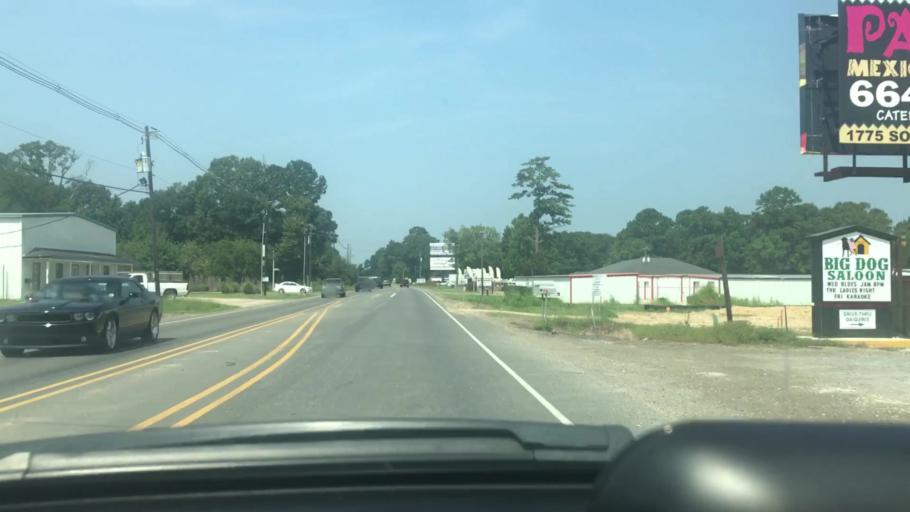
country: US
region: Louisiana
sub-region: Livingston Parish
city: Denham Springs
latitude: 30.4839
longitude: -90.9351
